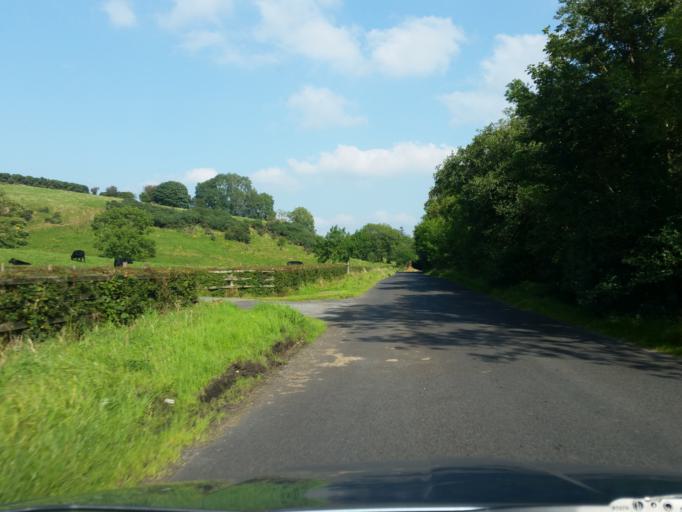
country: GB
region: Northern Ireland
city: Ballinamallard
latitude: 54.3822
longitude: -7.5759
